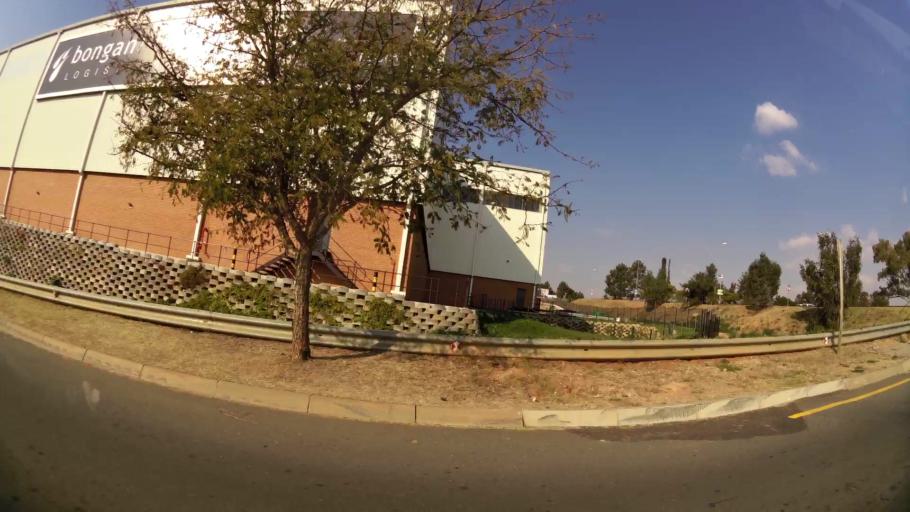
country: ZA
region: Gauteng
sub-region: City of Johannesburg Metropolitan Municipality
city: Modderfontein
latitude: -26.1052
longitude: 28.1429
